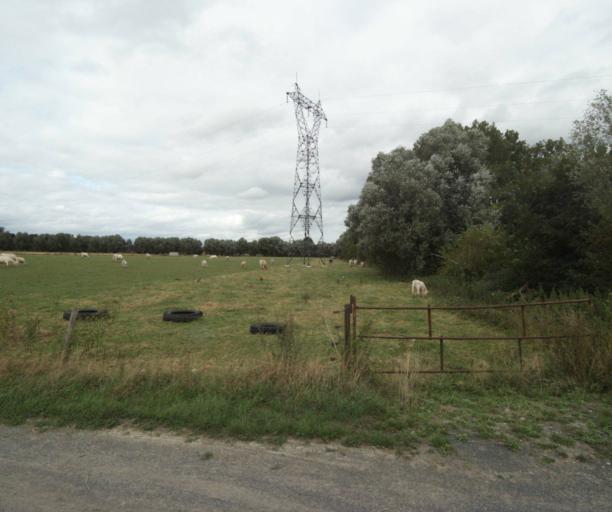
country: FR
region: Nord-Pas-de-Calais
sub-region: Departement du Nord
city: Sainghin-en-Melantois
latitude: 50.5645
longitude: 3.1769
